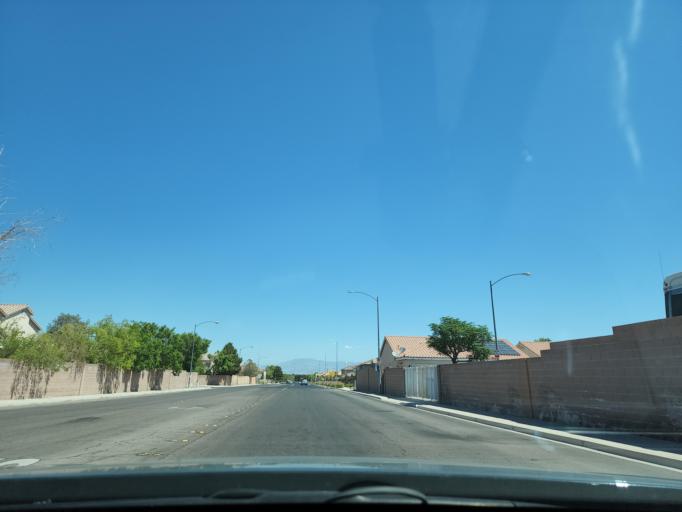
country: US
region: Nevada
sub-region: Clark County
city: Spring Valley
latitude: 36.0816
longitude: -115.2518
